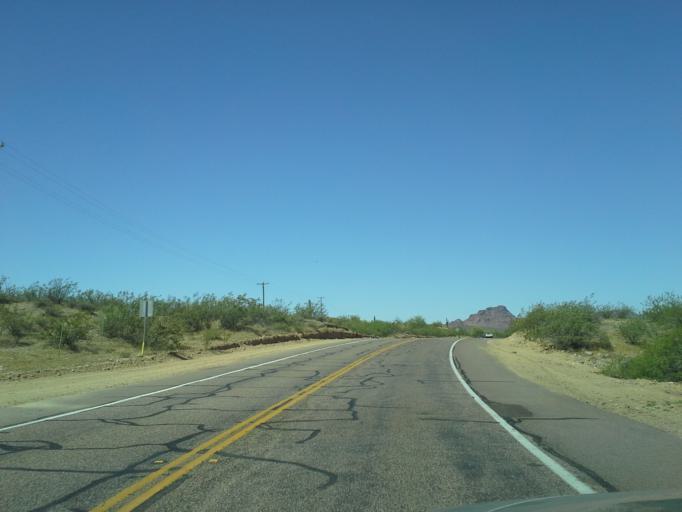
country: US
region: Arizona
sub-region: Pinal County
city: Apache Junction
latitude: 33.5494
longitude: -111.5852
